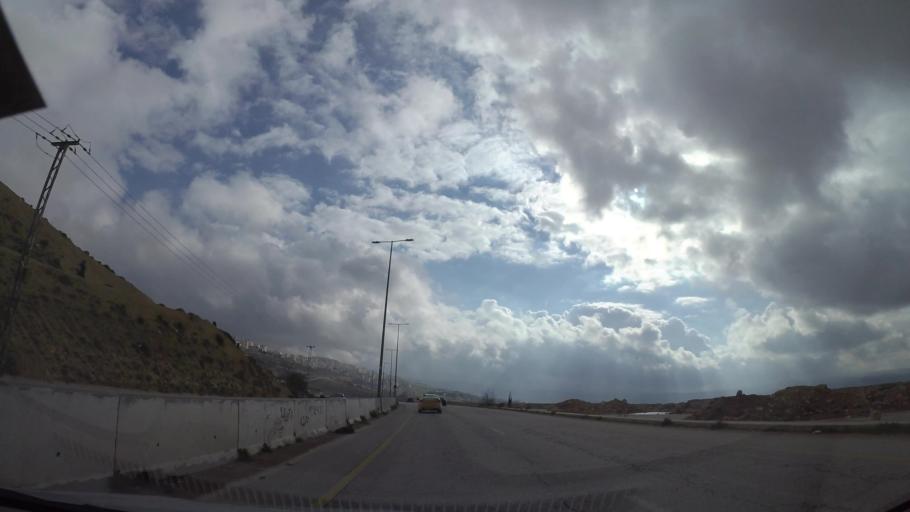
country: JO
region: Amman
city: Al Jubayhah
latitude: 32.0806
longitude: 35.8794
